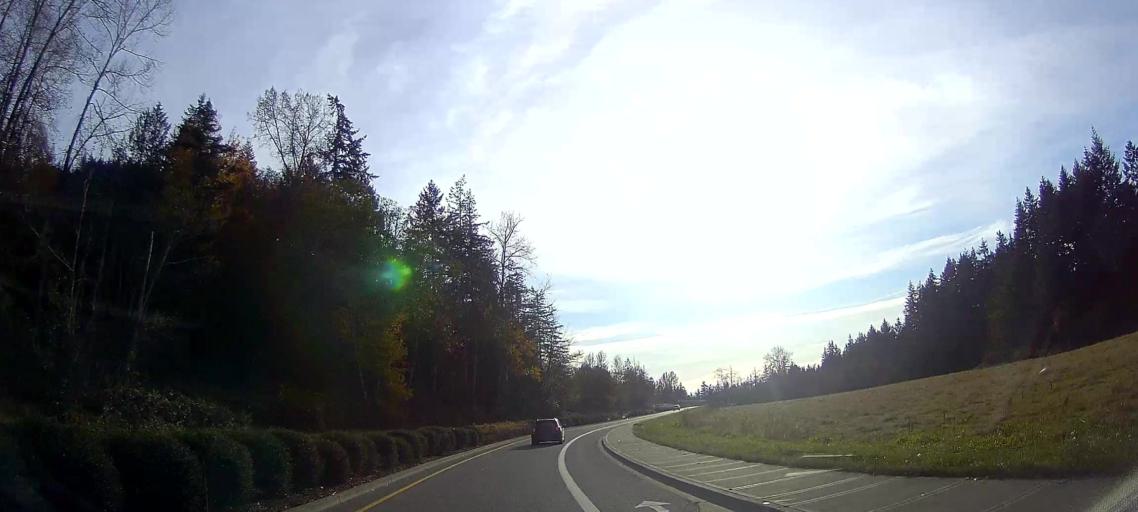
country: US
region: Washington
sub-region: Skagit County
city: Mount Vernon
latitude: 48.4041
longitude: -122.3139
